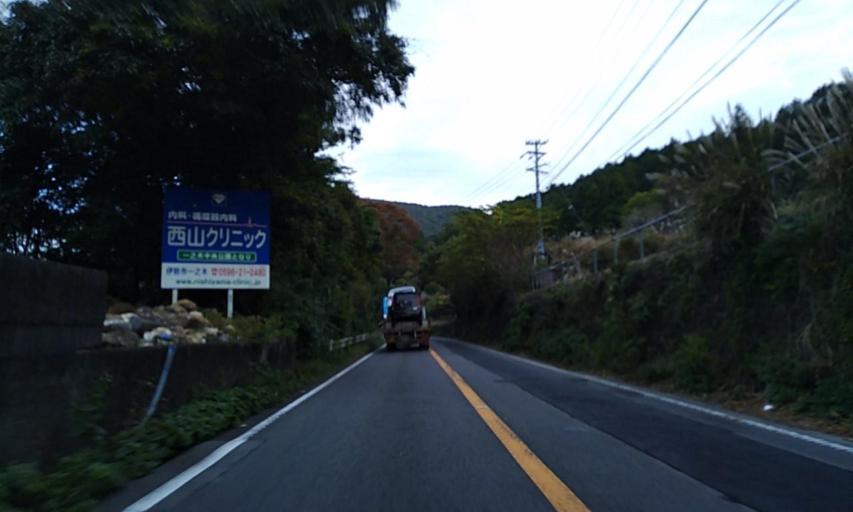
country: JP
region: Mie
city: Toba
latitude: 34.3924
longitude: 136.7873
